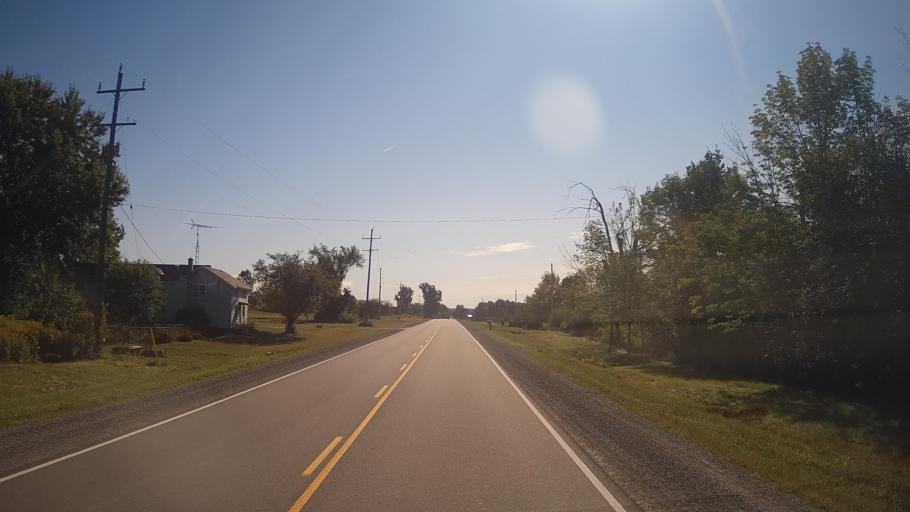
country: CA
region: Ontario
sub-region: Lanark County
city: Smiths Falls
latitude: 44.6248
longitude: -75.9760
